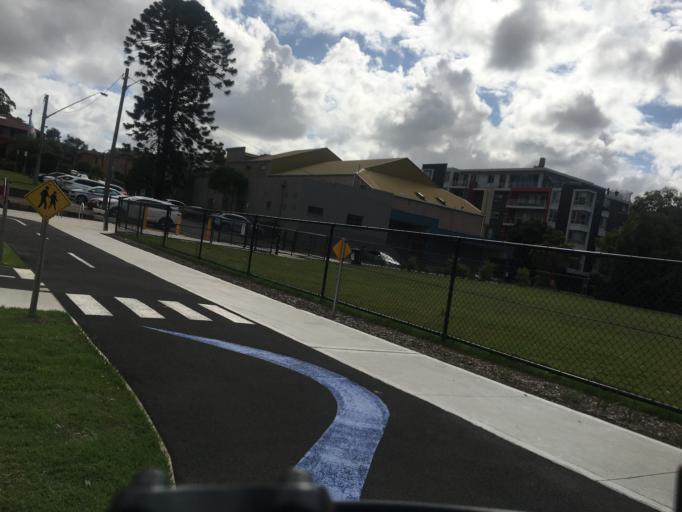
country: AU
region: New South Wales
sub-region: Ryde
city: East Ryde
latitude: -33.8145
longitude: 151.1084
